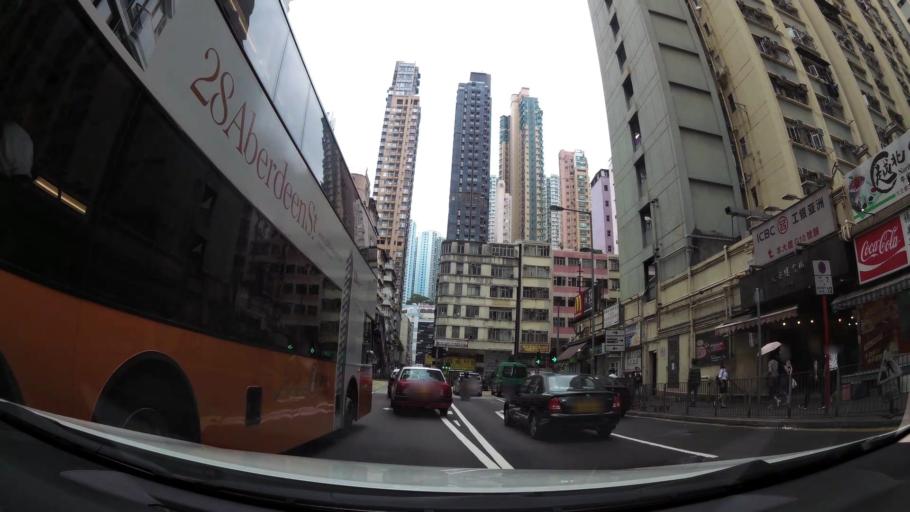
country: HK
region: Wanchai
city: Wan Chai
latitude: 22.2823
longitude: 114.2223
